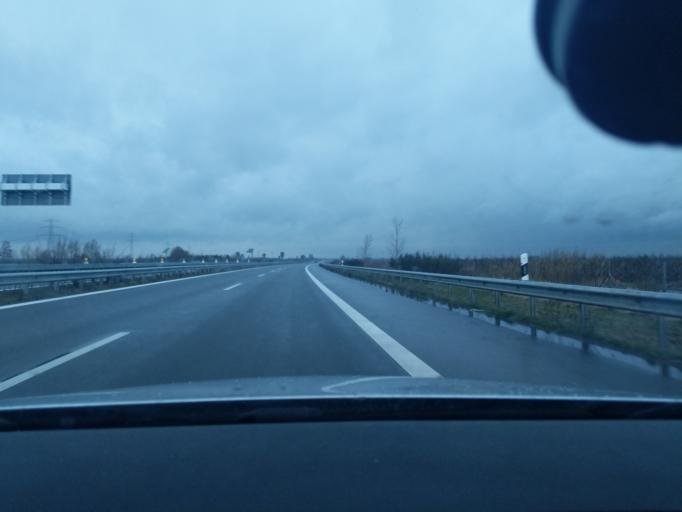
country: DE
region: Lower Saxony
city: Jork
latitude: 53.5024
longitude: 9.6547
